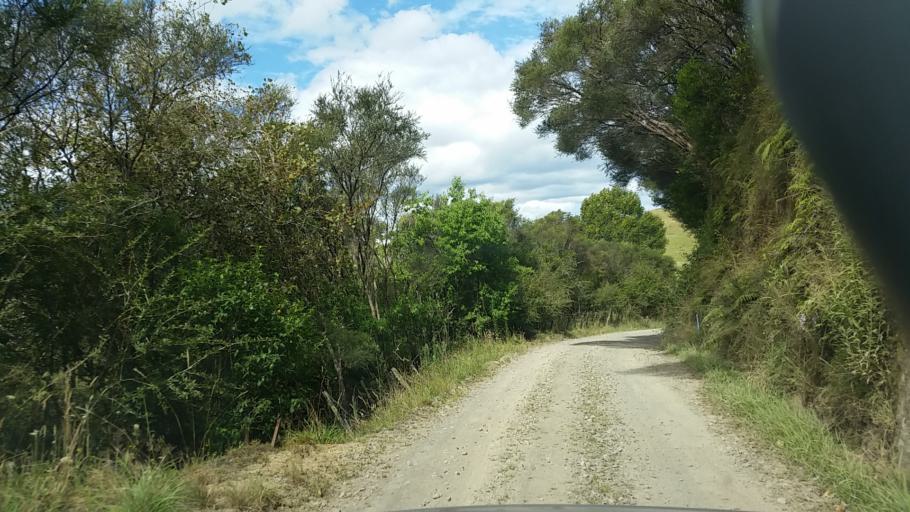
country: NZ
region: Taranaki
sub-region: South Taranaki District
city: Eltham
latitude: -39.2536
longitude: 174.5677
